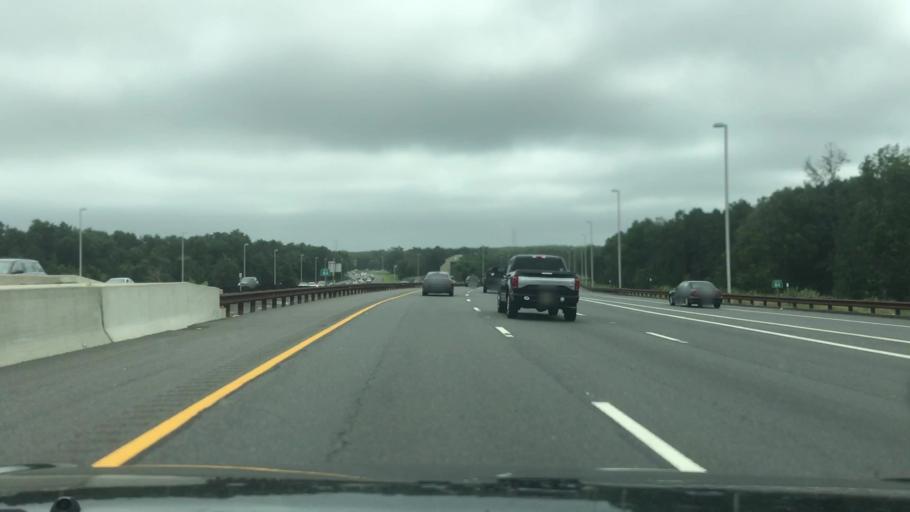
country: US
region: New Jersey
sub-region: Ocean County
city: Silver Ridge
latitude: 39.9872
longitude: -74.2113
